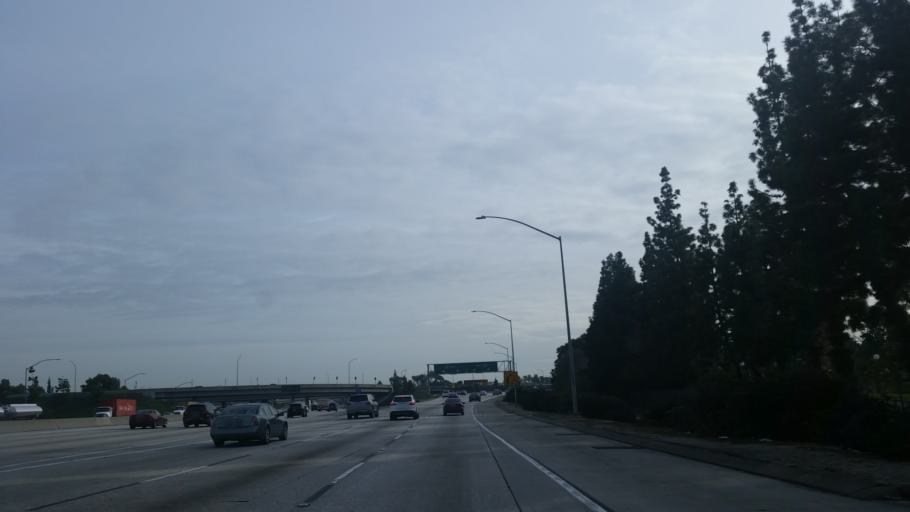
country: US
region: California
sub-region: Los Angeles County
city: Bellflower
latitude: 33.8804
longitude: -118.1041
